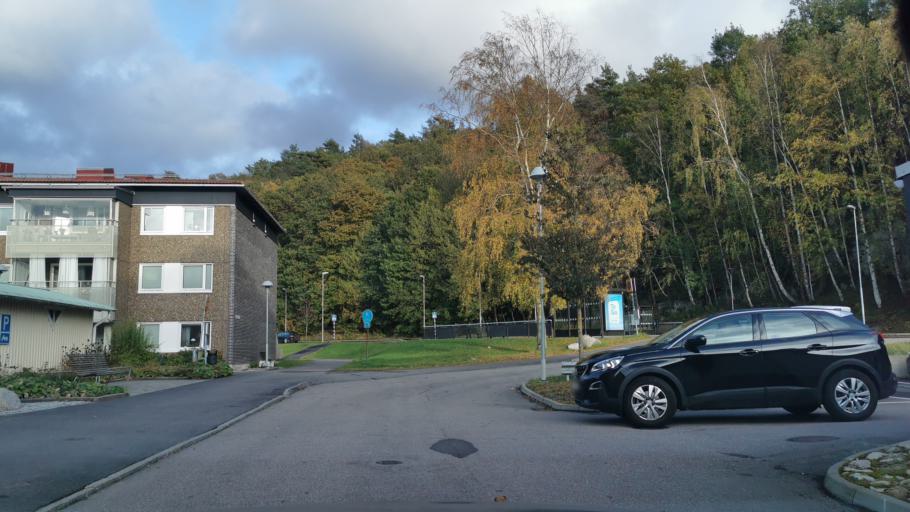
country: SE
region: Vaestra Goetaland
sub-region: Partille Kommun
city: Partille
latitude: 57.7188
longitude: 12.0810
